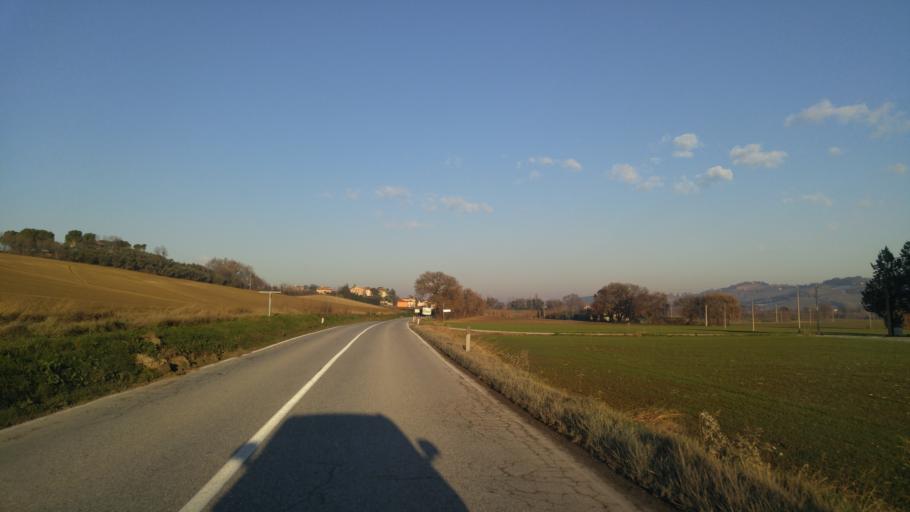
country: IT
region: The Marches
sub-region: Provincia di Pesaro e Urbino
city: Monte Porzio
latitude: 43.6831
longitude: 13.0357
